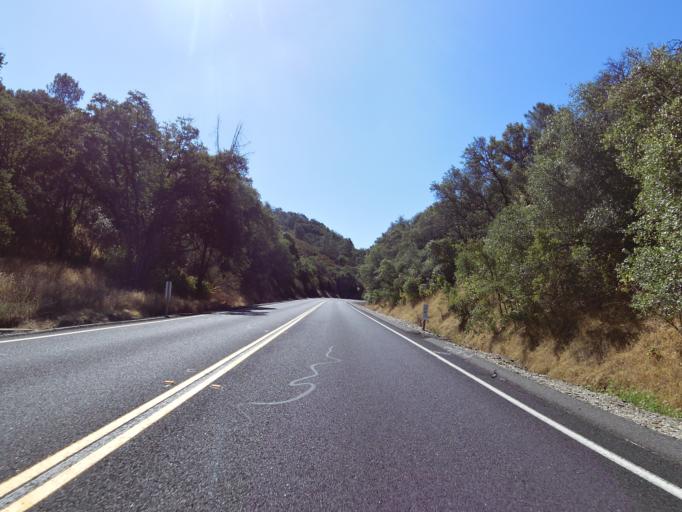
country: US
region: California
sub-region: Tuolumne County
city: Tuolumne City
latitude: 37.7115
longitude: -120.2060
